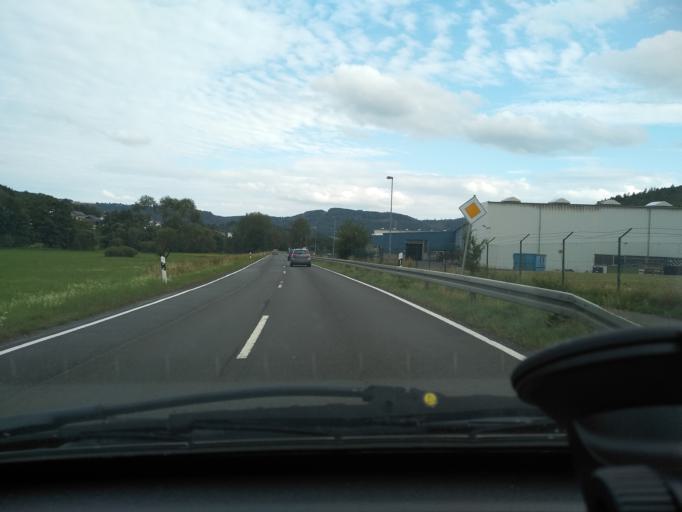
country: DE
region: Hesse
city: Dillenburg
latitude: 50.8239
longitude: 8.3340
